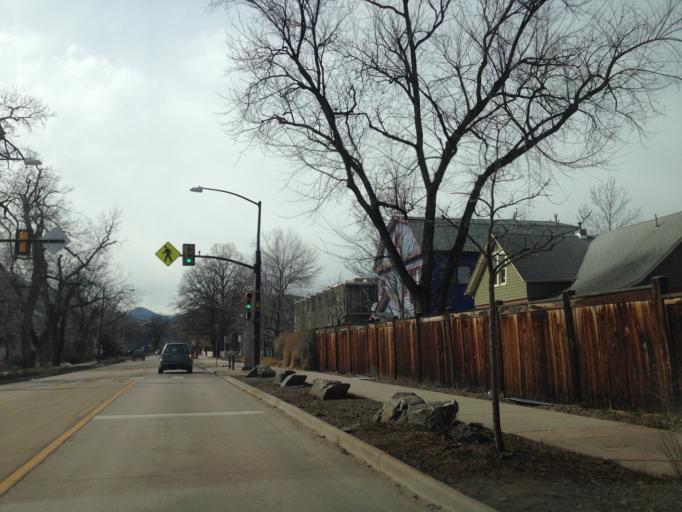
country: US
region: Colorado
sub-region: Boulder County
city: Boulder
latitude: 40.0146
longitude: -105.2666
